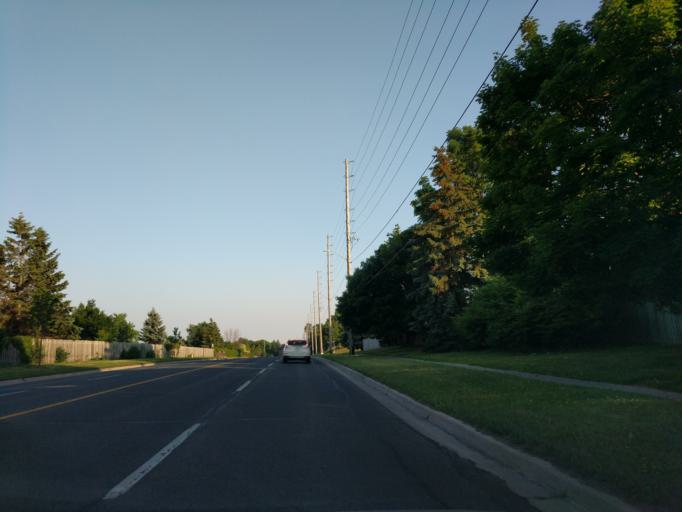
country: CA
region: Ontario
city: Oshawa
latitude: 43.9058
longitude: -78.8998
